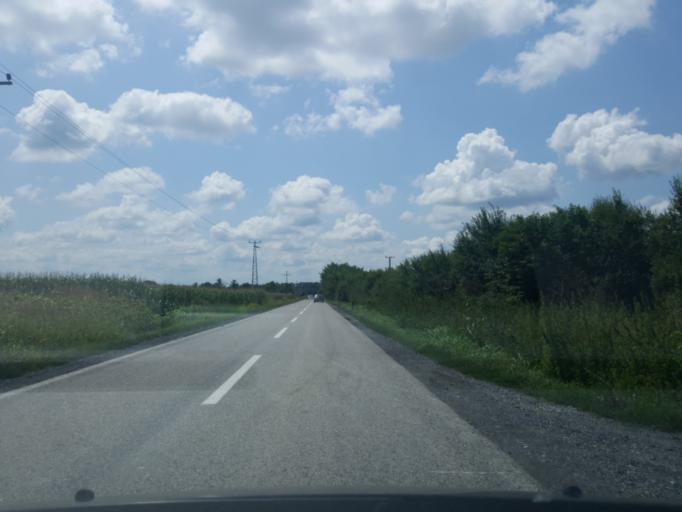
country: RS
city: Metkovic
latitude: 44.8675
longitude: 19.5466
